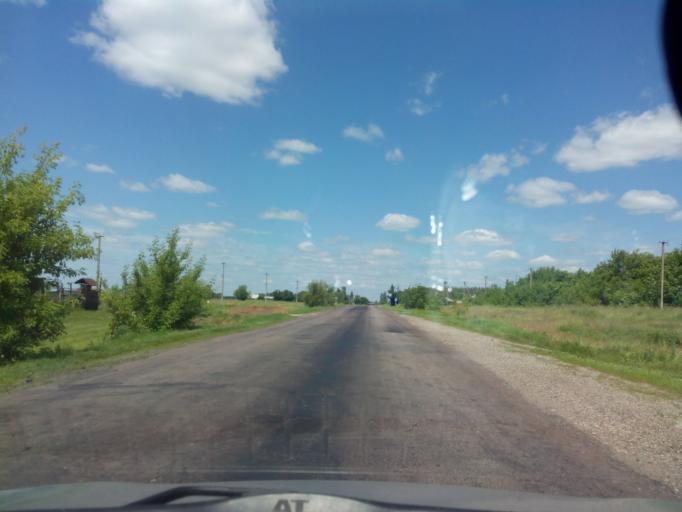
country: RU
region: Tambov
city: Zherdevka
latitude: 51.7307
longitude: 41.5167
